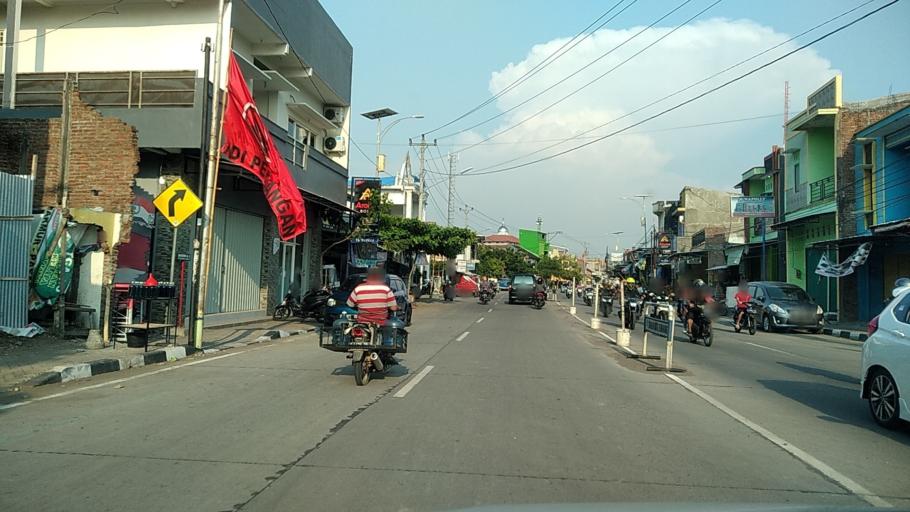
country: ID
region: Central Java
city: Semarang
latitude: -6.9856
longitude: 110.4453
